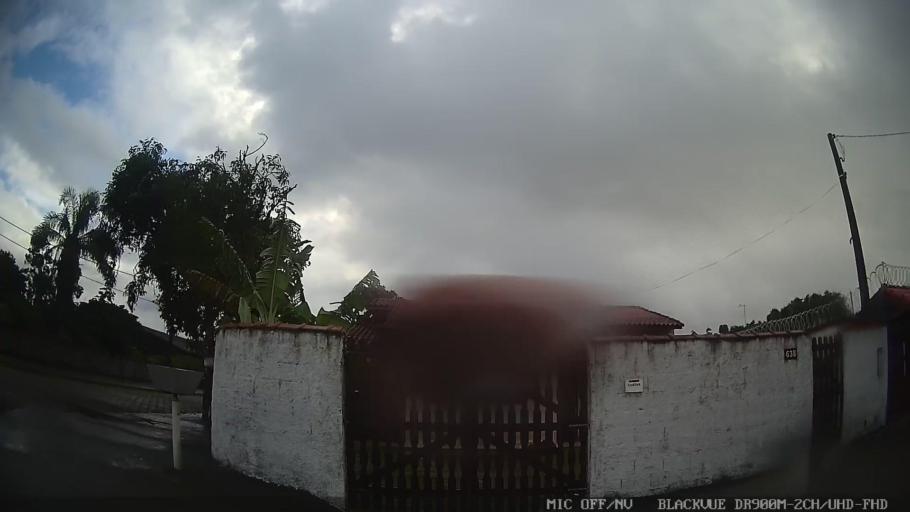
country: BR
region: Sao Paulo
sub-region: Itanhaem
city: Itanhaem
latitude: -24.2386
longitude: -46.8904
